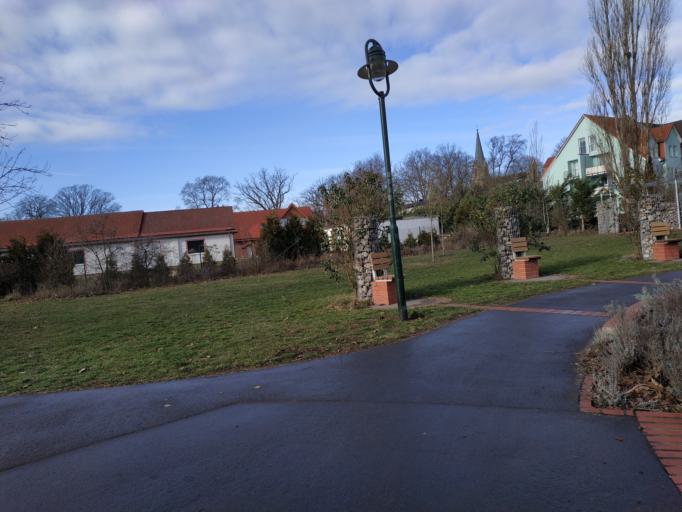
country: DE
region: Brandenburg
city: Petershagen
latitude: 52.5375
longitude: 13.8178
